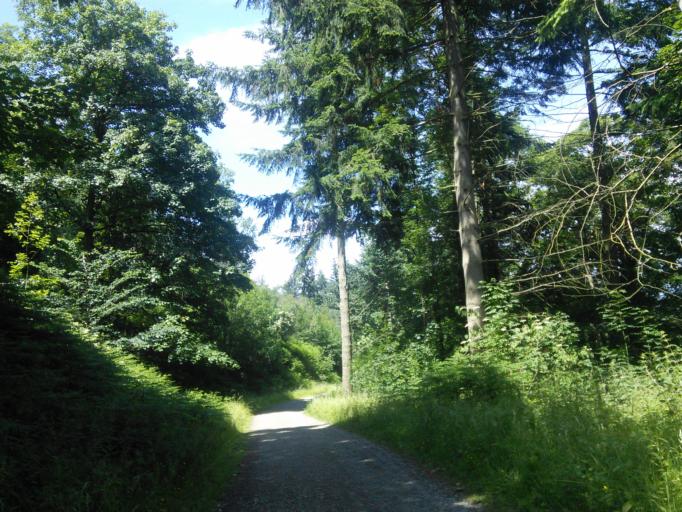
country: GB
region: England
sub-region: Shropshire
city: Pant
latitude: 52.7259
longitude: -3.0368
